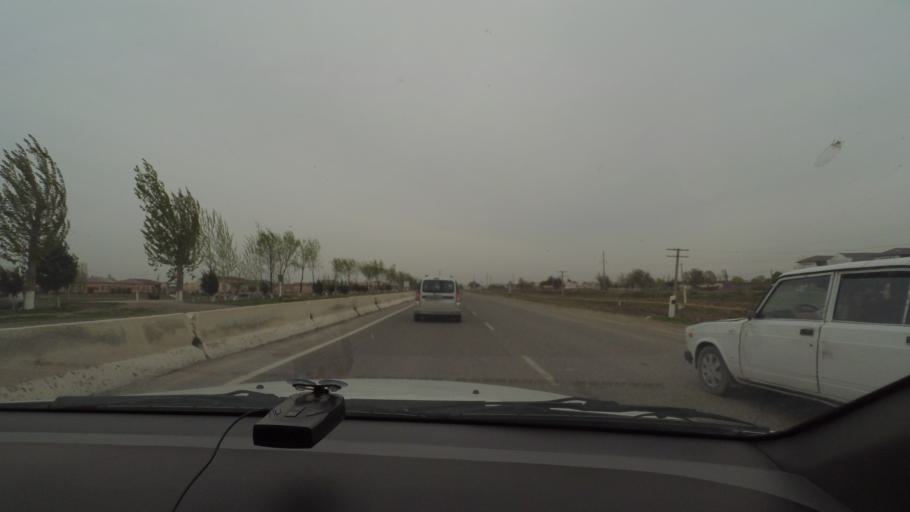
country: UZ
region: Sirdaryo
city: Guliston
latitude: 40.4898
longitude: 68.7293
